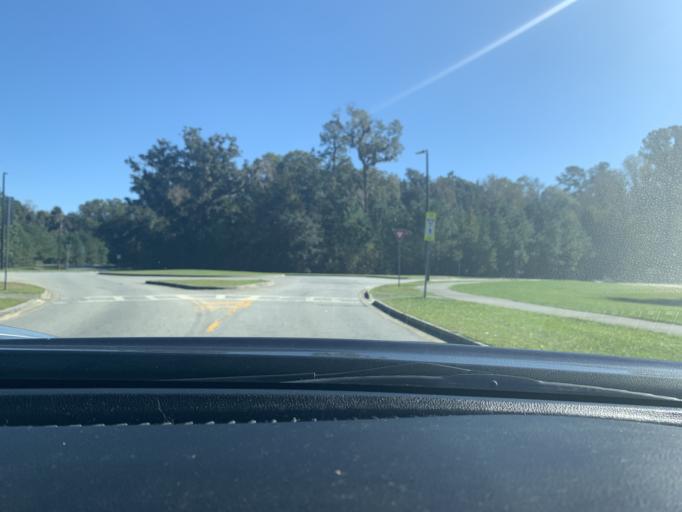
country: US
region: Georgia
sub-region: Chatham County
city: Pooler
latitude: 32.0856
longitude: -81.2735
